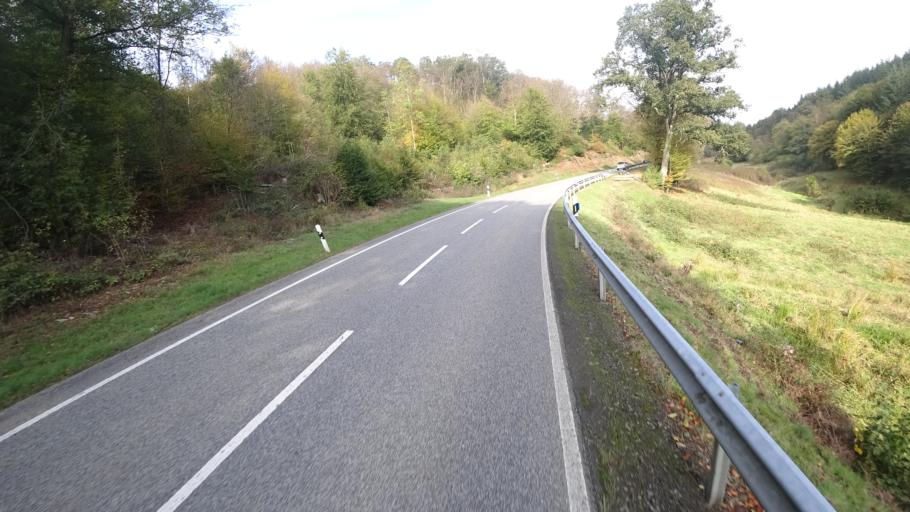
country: DE
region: Rheinland-Pfalz
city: Isselbach
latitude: 50.3976
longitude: 7.9105
